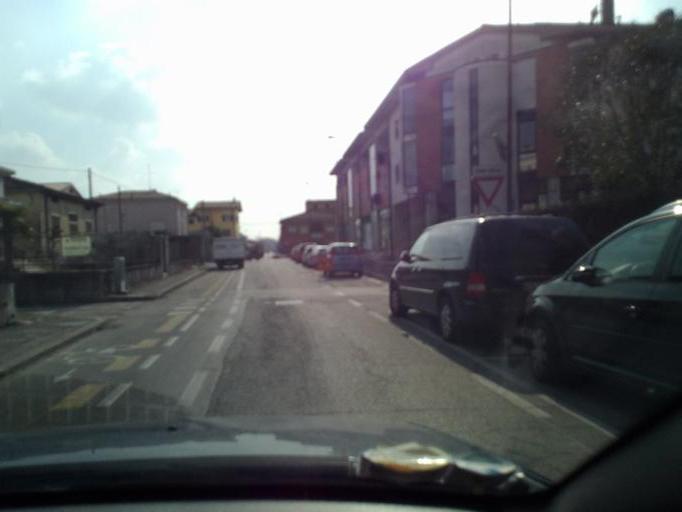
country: IT
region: Veneto
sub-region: Provincia di Verona
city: Villafranca di Verona
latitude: 45.3548
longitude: 10.8404
